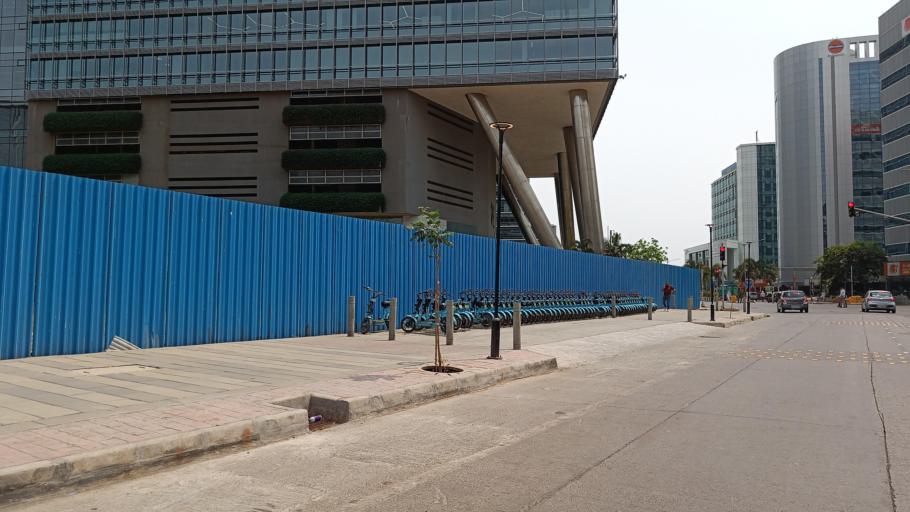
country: IN
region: Maharashtra
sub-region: Mumbai Suburban
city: Mumbai
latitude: 19.0615
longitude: 72.8645
